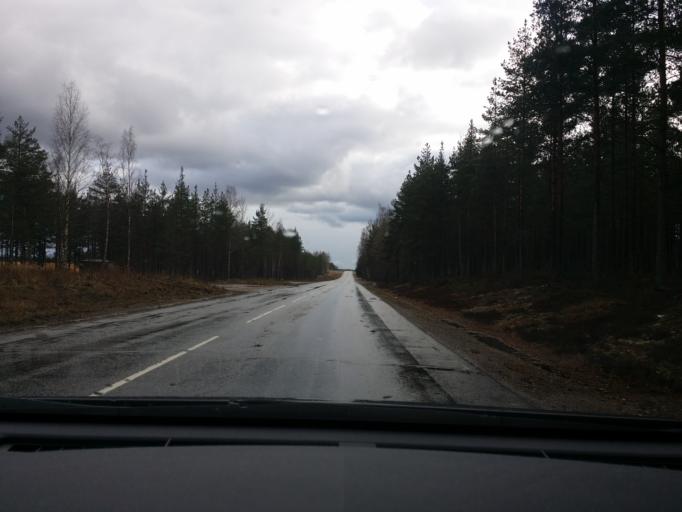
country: SE
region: Soedermanland
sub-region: Eskilstuna Kommun
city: Arla
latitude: 59.3391
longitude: 16.6909
